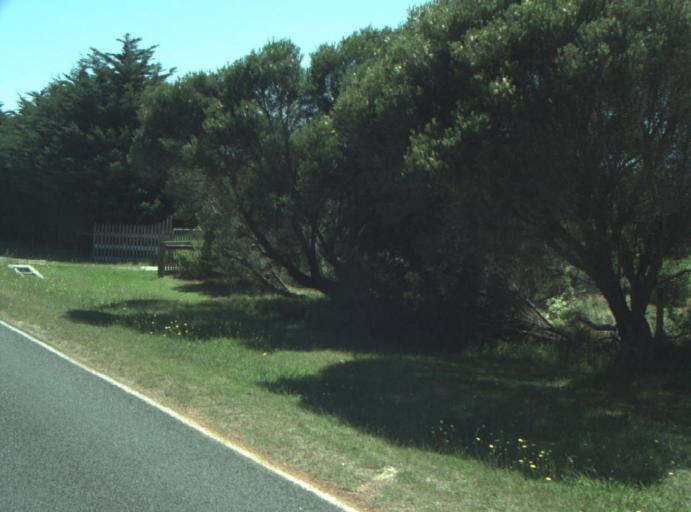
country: AU
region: Victoria
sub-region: Greater Geelong
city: Breakwater
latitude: -38.2296
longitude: 144.3548
